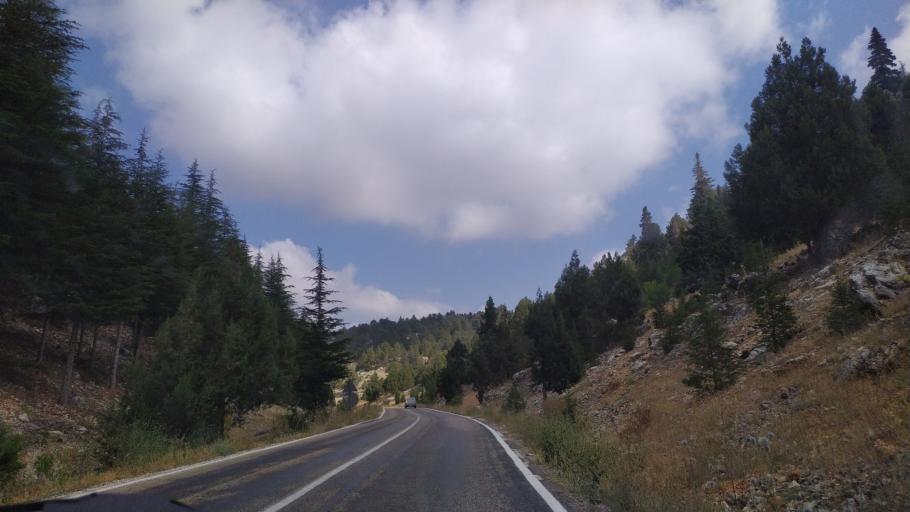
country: TR
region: Mersin
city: Kirobasi
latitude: 36.6127
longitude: 33.8795
